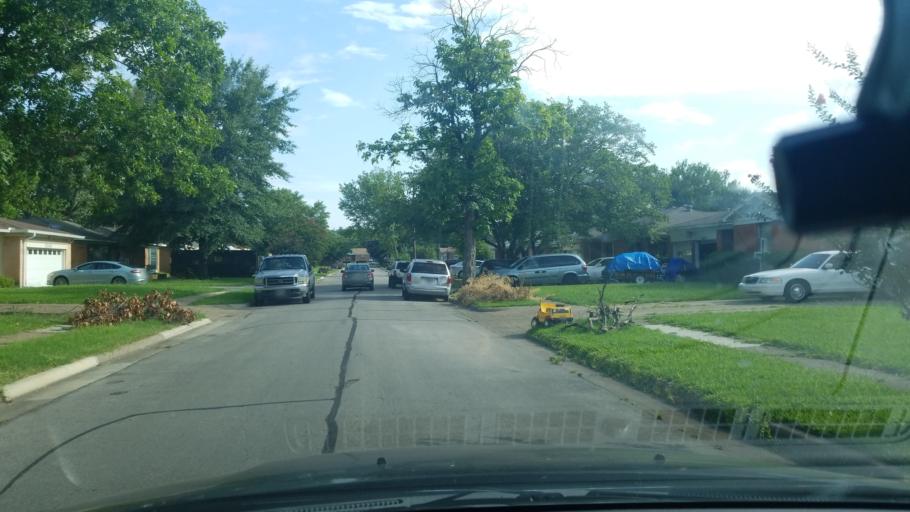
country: US
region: Texas
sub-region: Dallas County
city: Balch Springs
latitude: 32.7518
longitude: -96.6752
